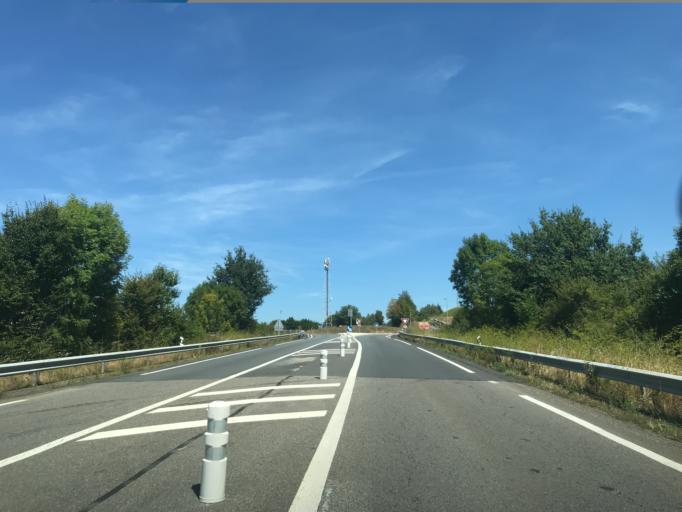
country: FR
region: Limousin
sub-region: Departement de la Correze
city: Tulle
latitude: 45.2825
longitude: 1.7975
